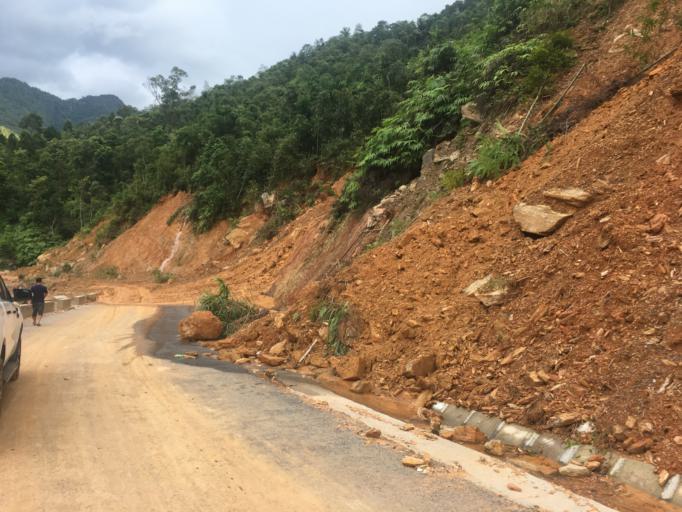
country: VN
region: Ha Giang
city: Thi Tran Tam Son
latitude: 22.9492
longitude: 105.0330
